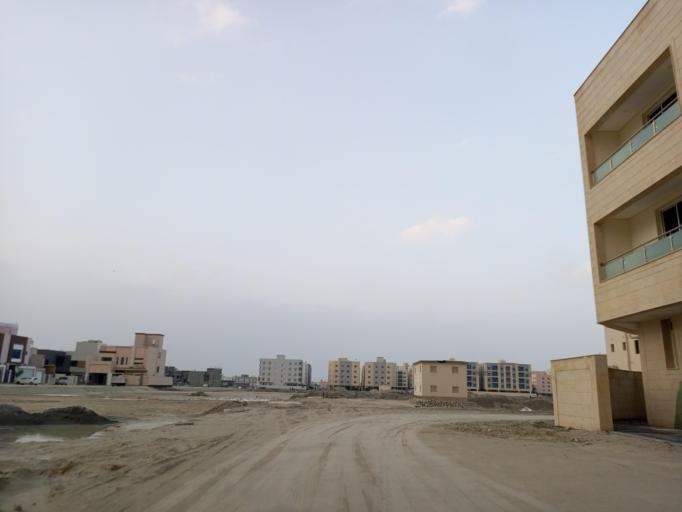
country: BH
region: Muharraq
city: Al Hadd
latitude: 26.2357
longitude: 50.6450
